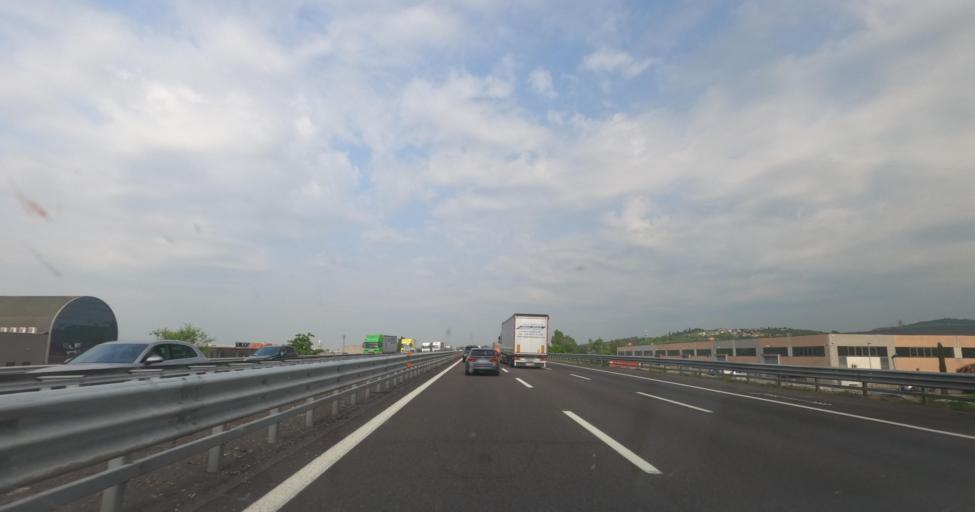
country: IT
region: Veneto
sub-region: Provincia di Verona
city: Caldierino-Rota
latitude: 45.4202
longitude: 11.1499
